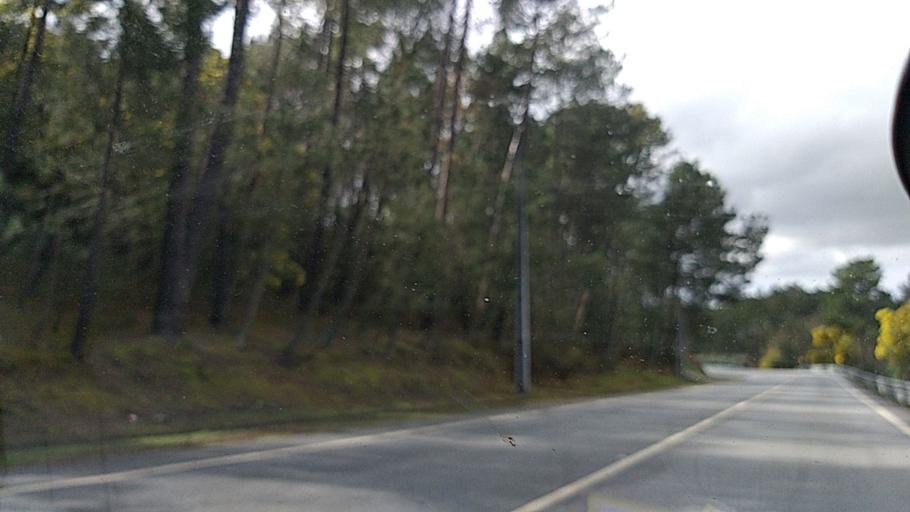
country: PT
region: Viseu
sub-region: Mangualde
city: Mangualde
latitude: 40.6545
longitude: -7.7313
